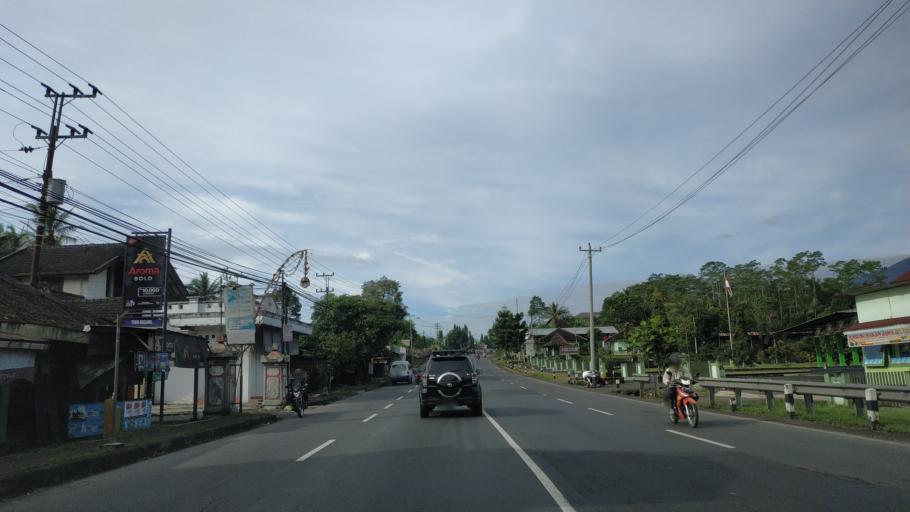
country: ID
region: Central Java
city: Salatiga
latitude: -7.3856
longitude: 110.5150
